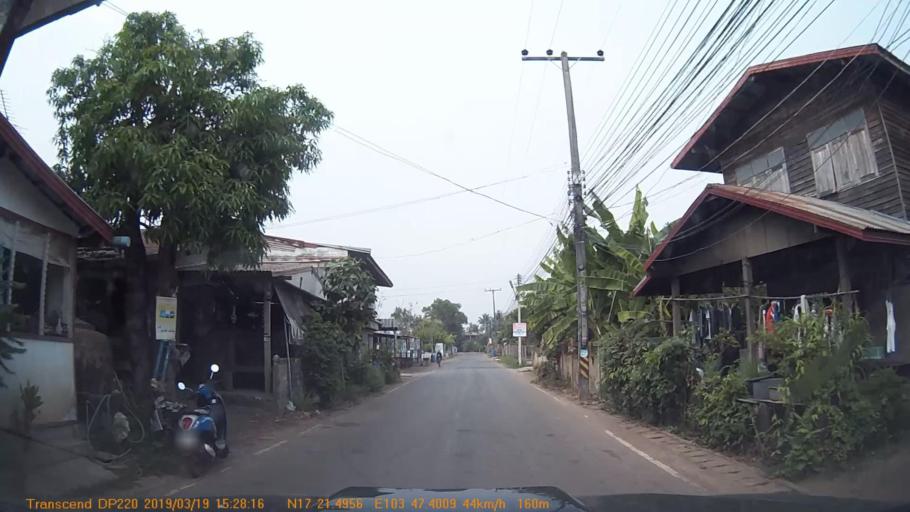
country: TH
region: Sakon Nakhon
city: Phanna Nikhom
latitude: 17.3584
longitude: 103.7901
